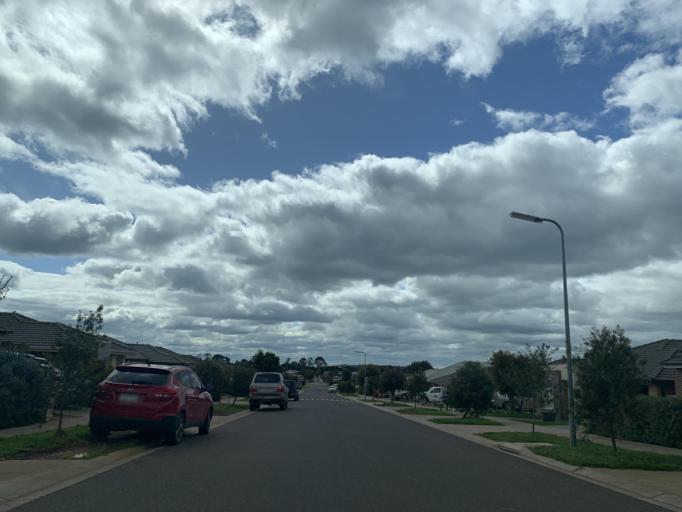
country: AU
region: Victoria
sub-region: Whittlesea
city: Whittlesea
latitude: -37.2930
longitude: 144.9354
